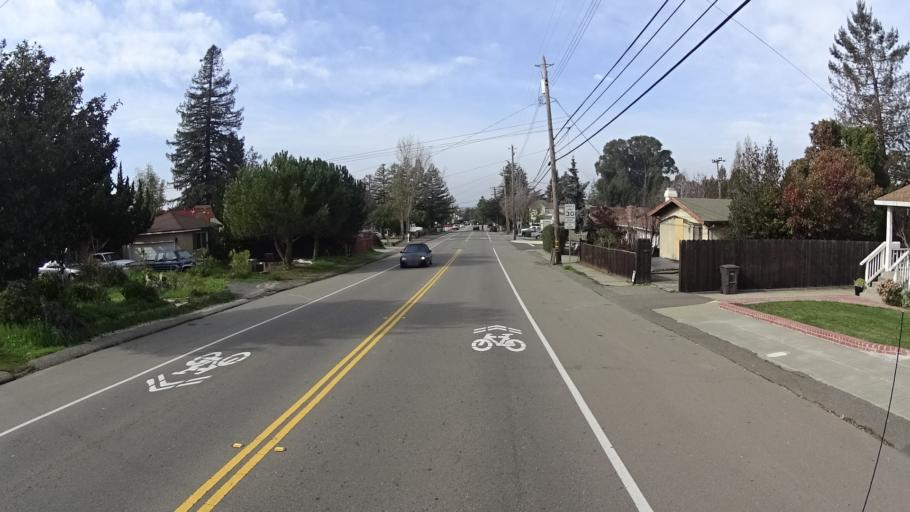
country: US
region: California
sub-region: Alameda County
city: Fairview
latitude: 37.6794
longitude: -122.0545
